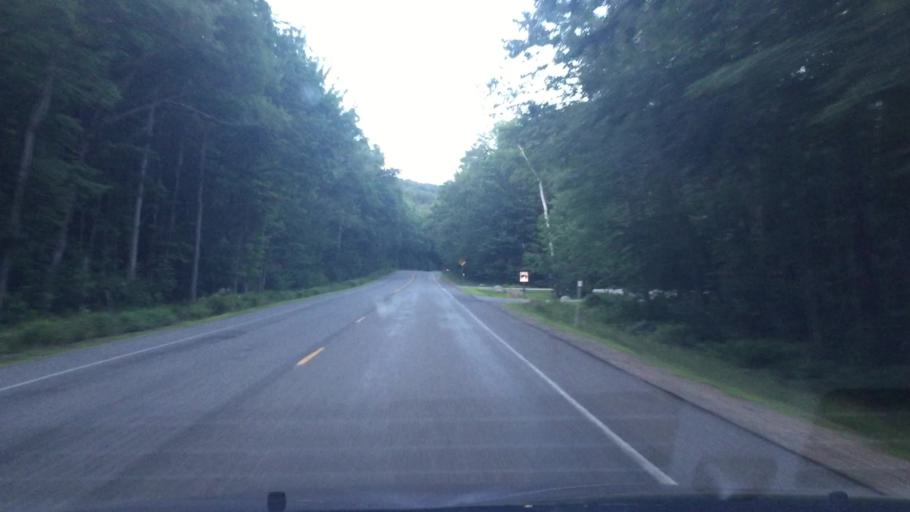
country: US
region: New Hampshire
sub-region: Grafton County
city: Woodstock
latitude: 44.0646
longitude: -71.6073
